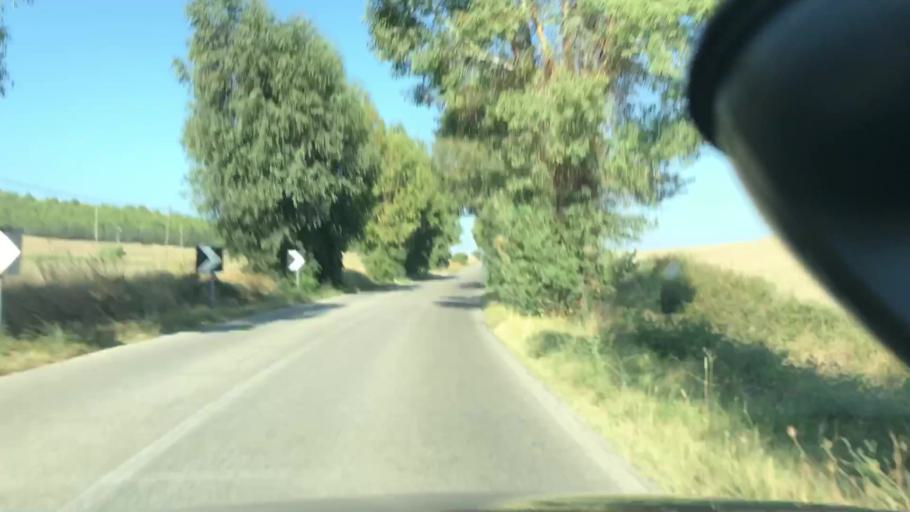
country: IT
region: Basilicate
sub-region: Provincia di Matera
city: La Martella
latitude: 40.6640
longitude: 16.4989
